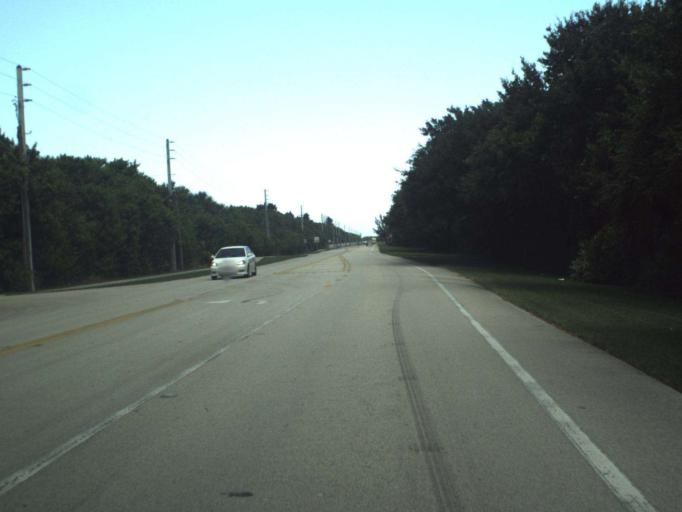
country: US
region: Florida
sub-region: Indian River County
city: Wabasso Beach
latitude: 27.7751
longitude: -80.4043
